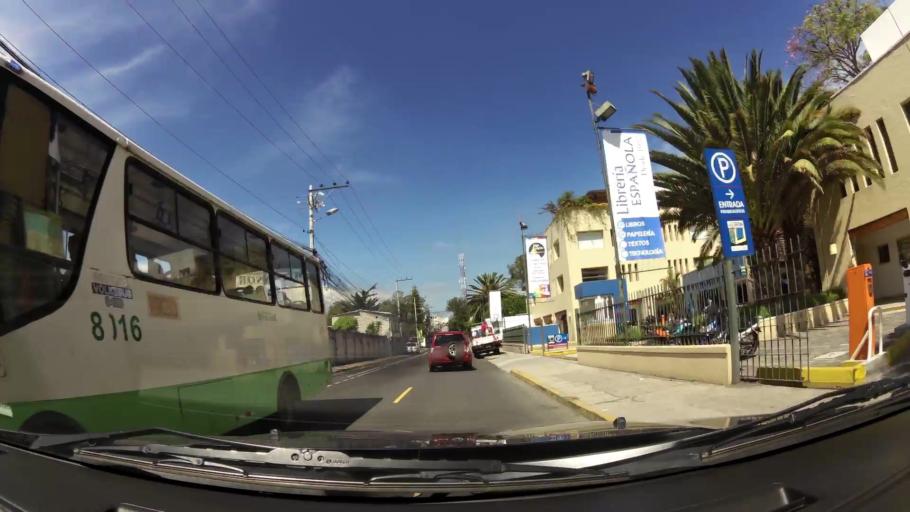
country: EC
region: Pichincha
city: Quito
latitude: -0.1976
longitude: -78.4311
